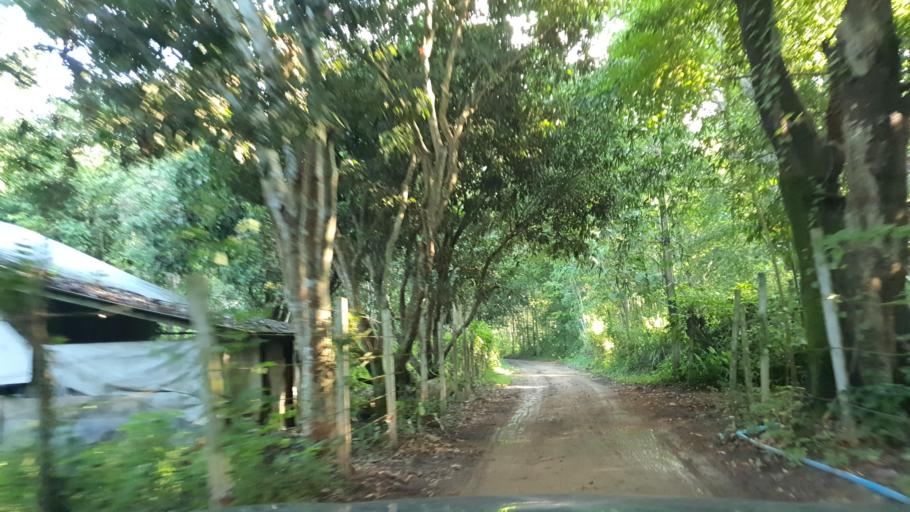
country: TH
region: Chiang Mai
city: Hang Dong
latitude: 18.7097
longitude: 98.8571
